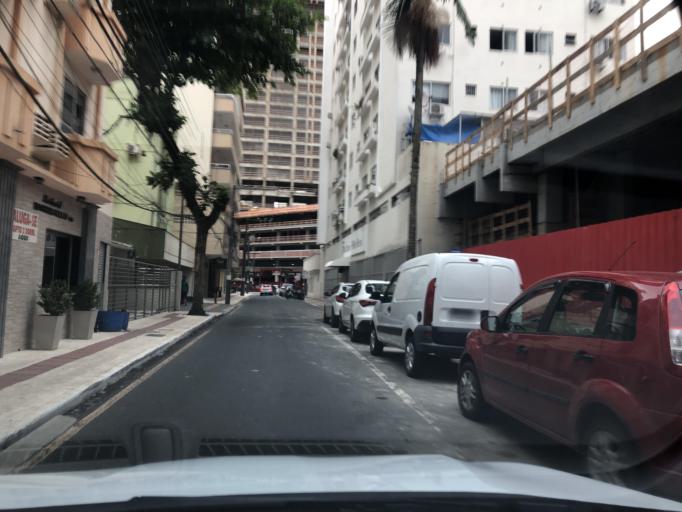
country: BR
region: Santa Catarina
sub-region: Balneario Camboriu
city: Balneario Camboriu
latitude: -27.0006
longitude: -48.6233
